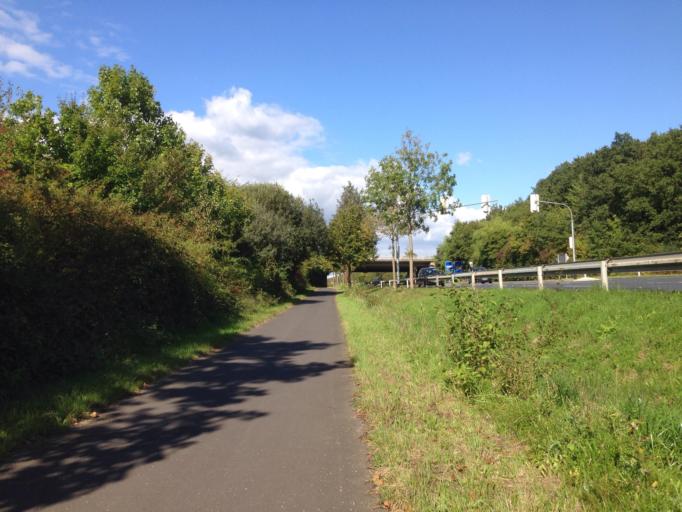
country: DE
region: Hesse
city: Lollar
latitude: 50.6221
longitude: 8.7065
